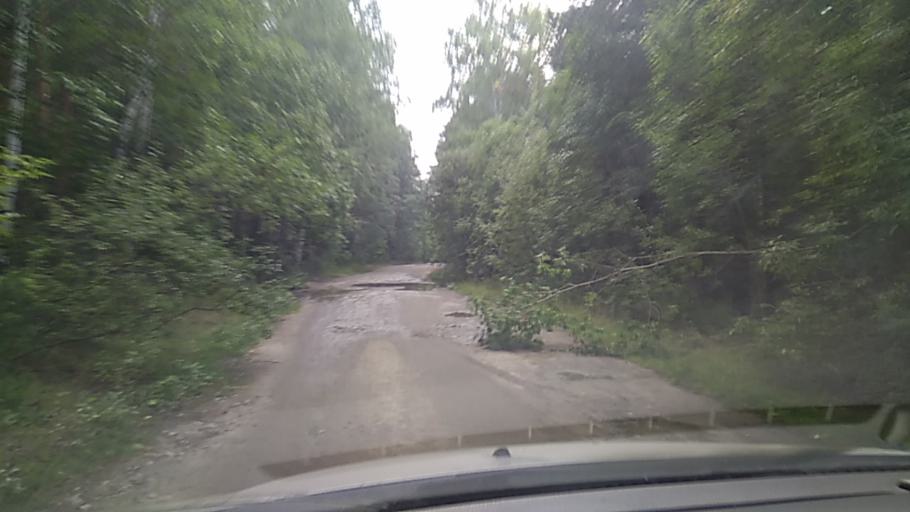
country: RU
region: Chelyabinsk
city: Kyshtym
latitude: 55.6779
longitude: 60.5855
